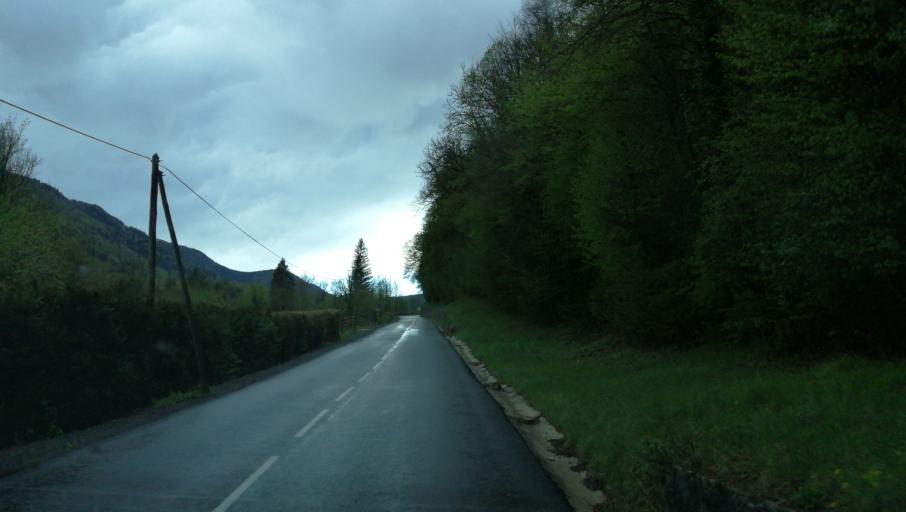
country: FR
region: Franche-Comte
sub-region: Departement du Jura
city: Saint-Claude
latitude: 46.3713
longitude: 5.8684
